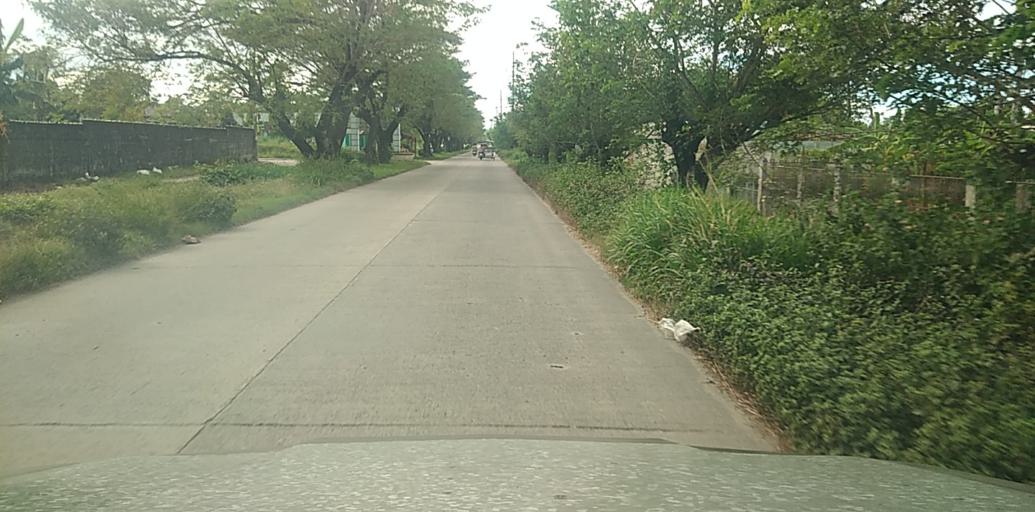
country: PH
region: Central Luzon
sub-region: Province of Pampanga
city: Pandacaqui
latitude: 15.1775
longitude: 120.6613
